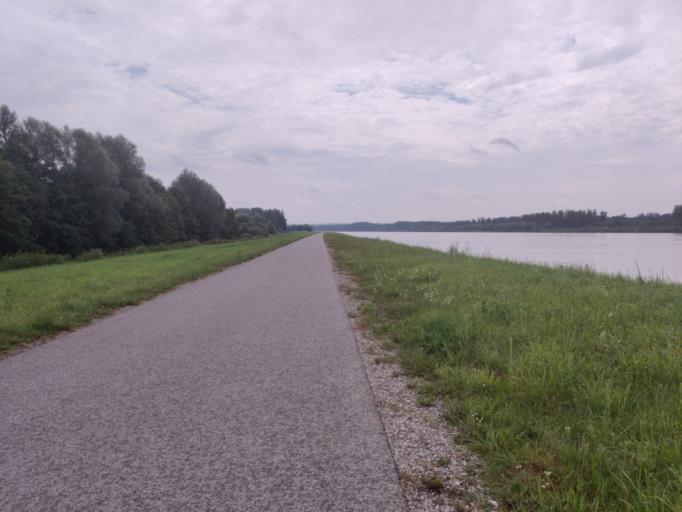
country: AT
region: Upper Austria
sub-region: Politischer Bezirk Perg
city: Perg
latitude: 48.2091
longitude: 14.6010
